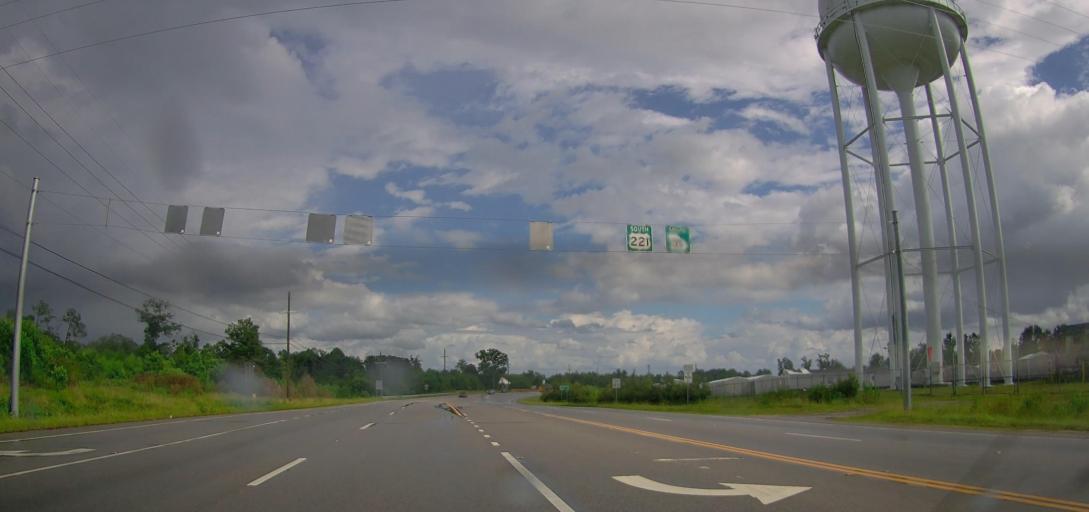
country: US
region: Georgia
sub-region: Coffee County
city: Douglas
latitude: 31.5077
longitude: -82.8295
